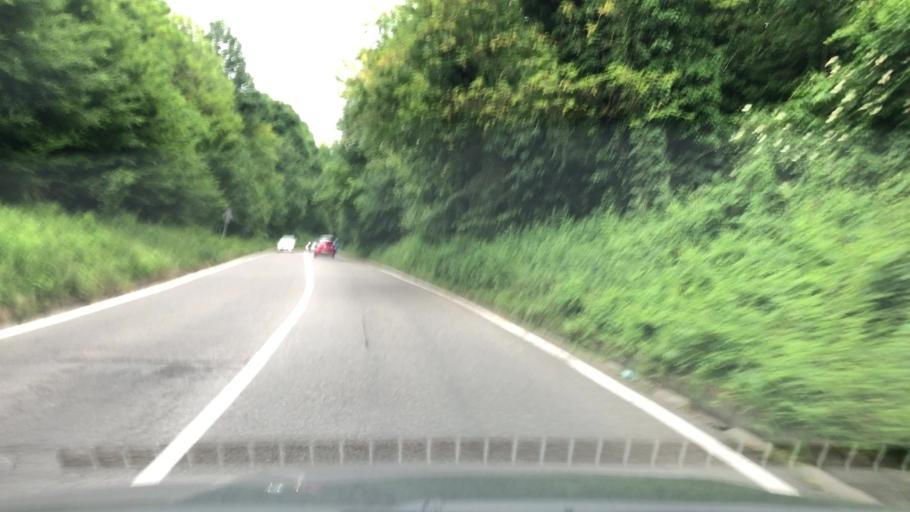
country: IT
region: Lombardy
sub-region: Provincia di Como
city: Fino Mornasco
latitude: 45.7406
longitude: 9.0661
